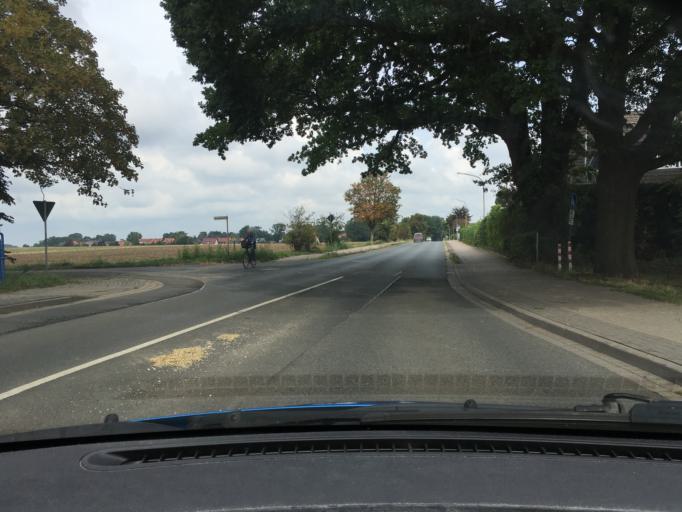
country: DE
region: Lower Saxony
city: Garbsen
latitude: 52.4357
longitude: 9.5742
